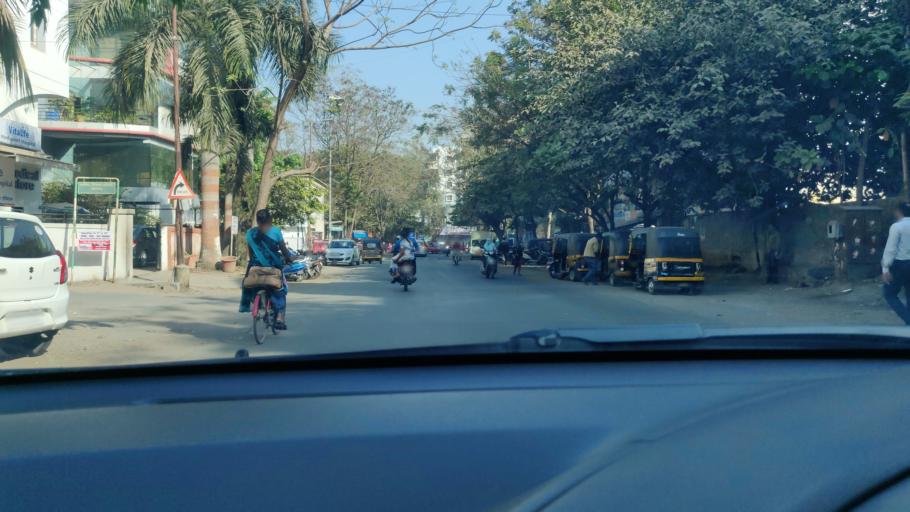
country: IN
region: Maharashtra
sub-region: Pune Division
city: Khadki
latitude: 18.5647
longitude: 73.8025
